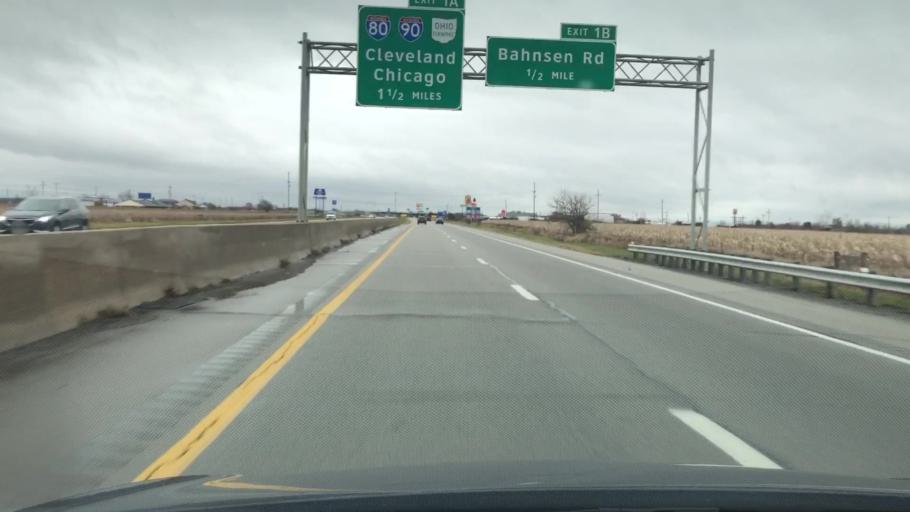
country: US
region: Ohio
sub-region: Wood County
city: Millbury
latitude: 41.5475
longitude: -83.4618
